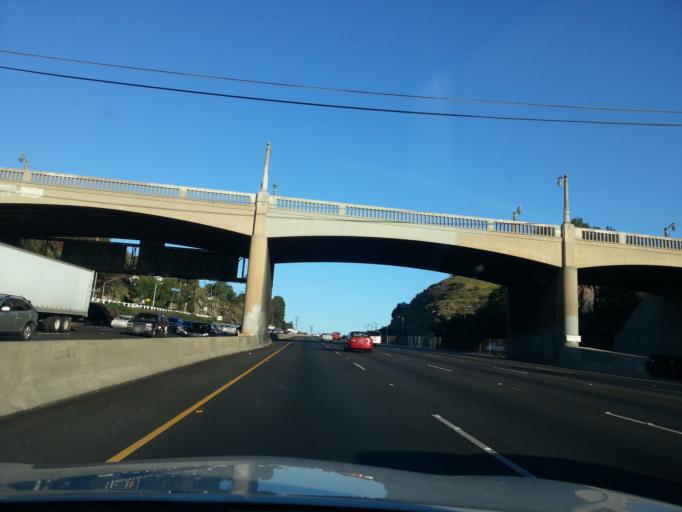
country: US
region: California
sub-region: Los Angeles County
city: Universal City
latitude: 34.1229
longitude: -118.3414
